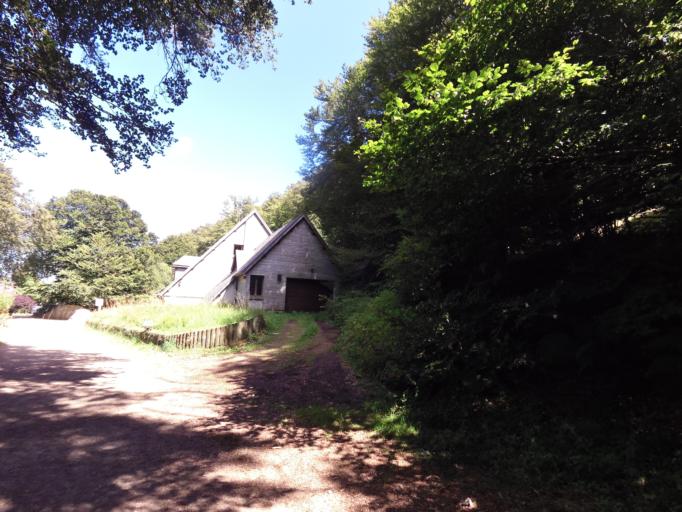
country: FR
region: Auvergne
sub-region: Departement du Puy-de-Dome
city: Mont-Dore
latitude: 45.5399
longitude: 2.8604
